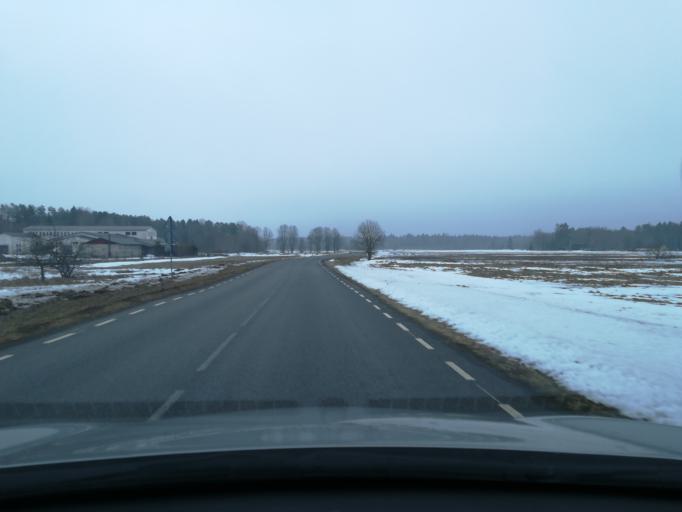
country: EE
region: Harju
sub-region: Kuusalu vald
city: Kuusalu
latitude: 59.4713
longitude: 25.5641
